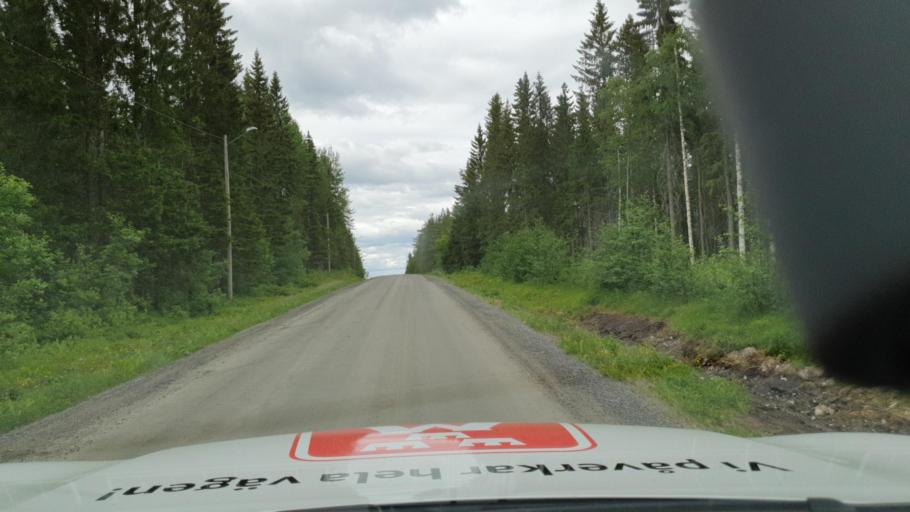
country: SE
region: Vaesterbotten
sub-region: Nordmalings Kommun
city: Nordmaling
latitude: 63.6941
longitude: 19.4436
